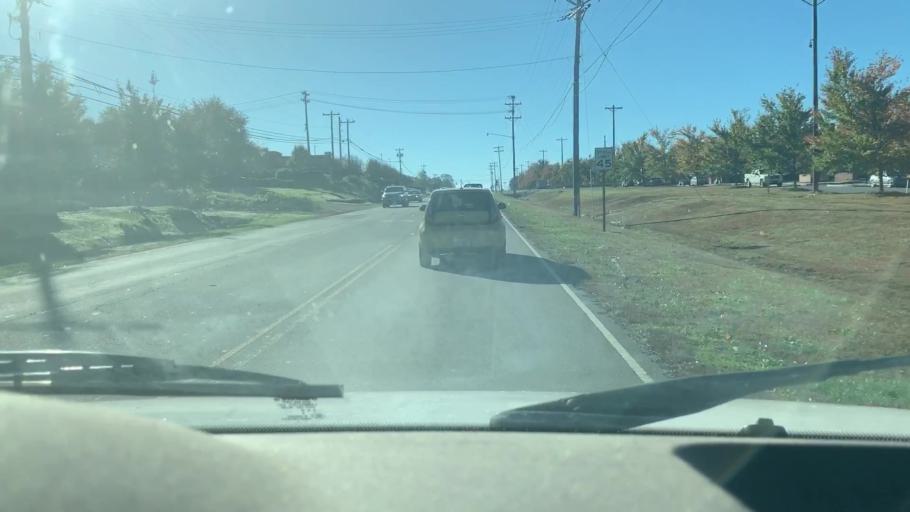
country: US
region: North Carolina
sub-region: Mecklenburg County
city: Huntersville
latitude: 35.4137
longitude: -80.8561
